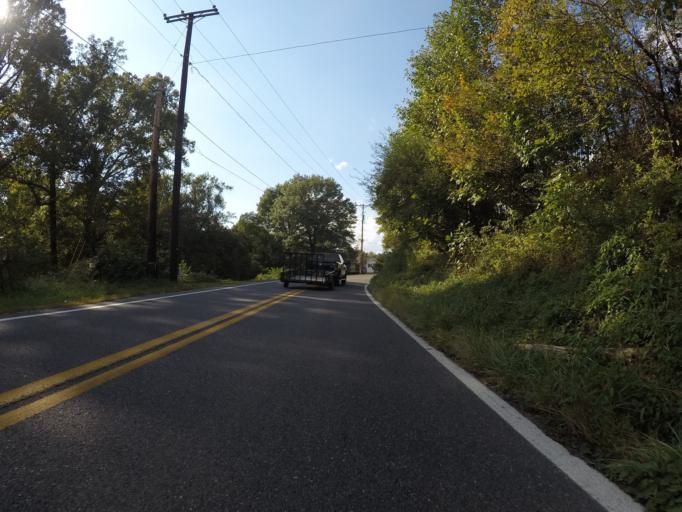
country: US
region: Ohio
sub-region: Lawrence County
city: Burlington
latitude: 38.3530
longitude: -82.5028
